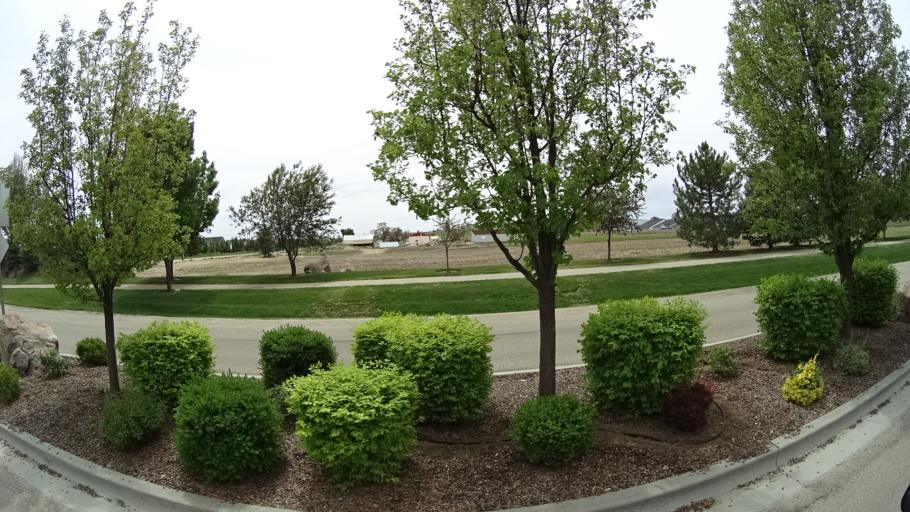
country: US
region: Idaho
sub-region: Ada County
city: Meridian
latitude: 43.5535
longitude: -116.3550
